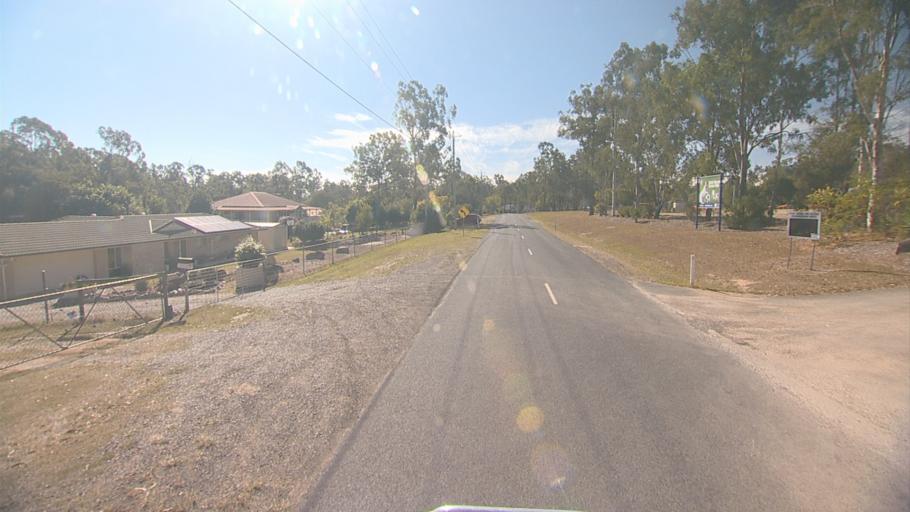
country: AU
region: Queensland
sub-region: Logan
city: North Maclean
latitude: -27.7281
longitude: 152.9618
